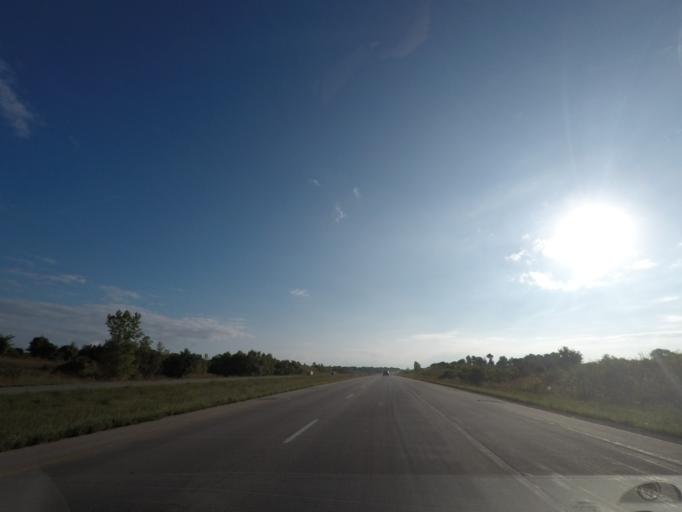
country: US
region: Iowa
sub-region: Warren County
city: Carlisle
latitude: 41.5080
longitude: -93.5638
